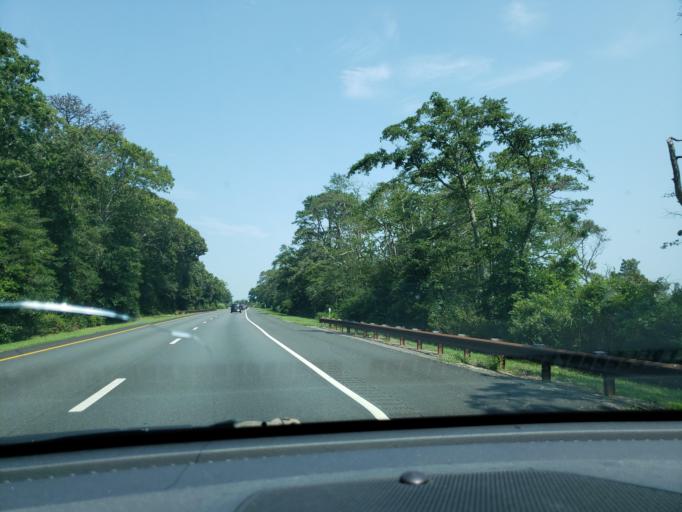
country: US
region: New Jersey
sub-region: Cape May County
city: Ocean City
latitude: 39.2701
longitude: -74.6353
